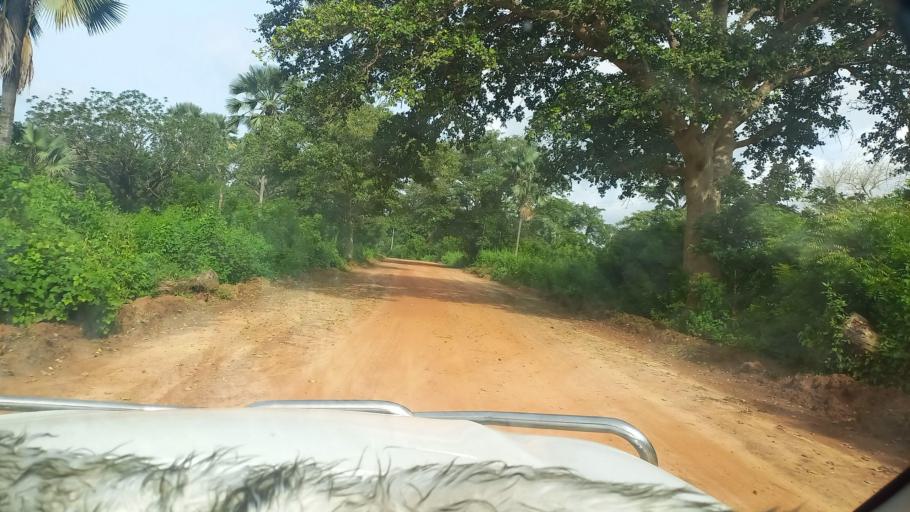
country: SN
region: Ziguinchor
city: Ziguinchor
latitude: 12.6679
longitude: -16.2681
